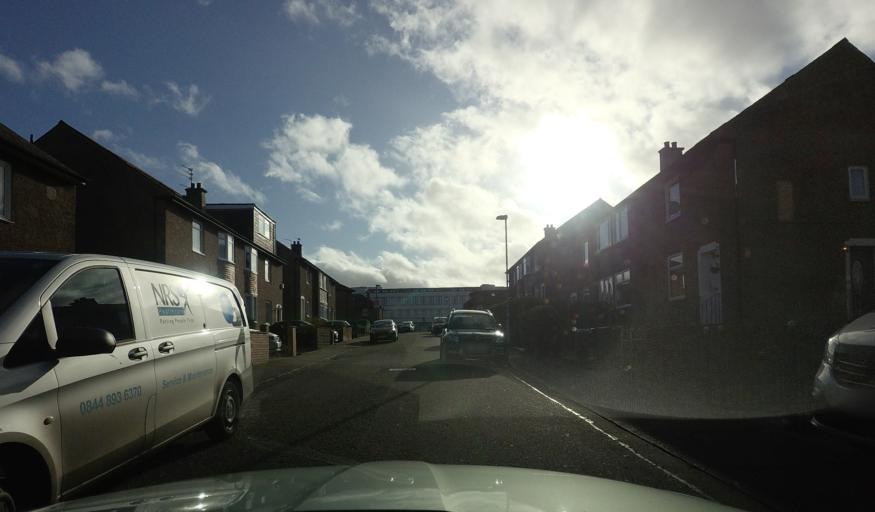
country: GB
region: Scotland
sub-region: Edinburgh
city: Edinburgh
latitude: 55.9731
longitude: -3.2368
